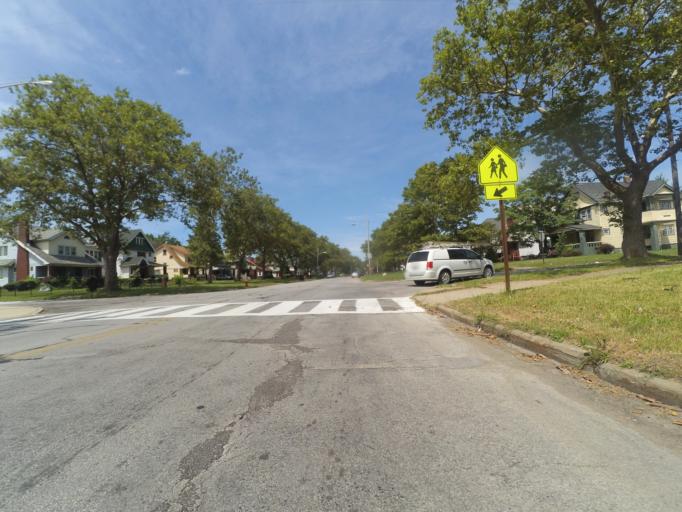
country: US
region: Ohio
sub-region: Cuyahoga County
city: Garfield Heights
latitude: 41.4614
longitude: -81.6073
